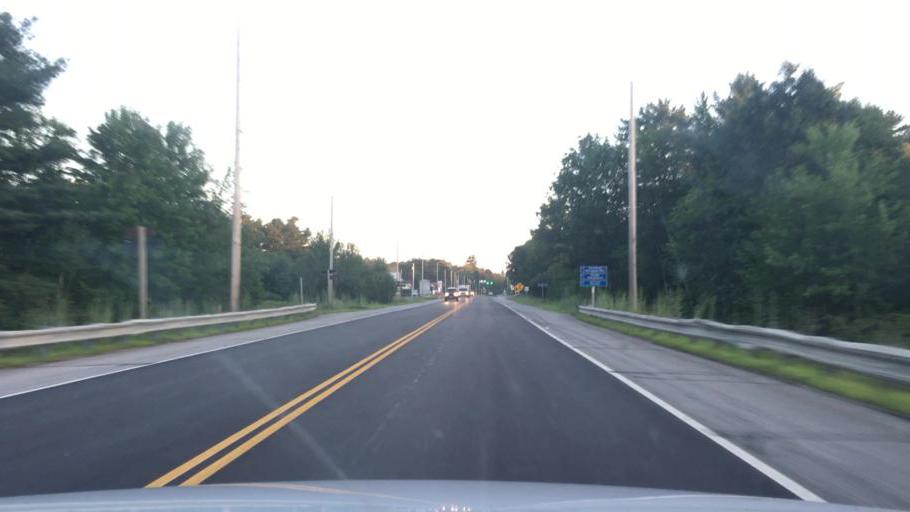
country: US
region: Maine
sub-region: Androscoggin County
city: Turner
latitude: 44.2548
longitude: -70.2592
